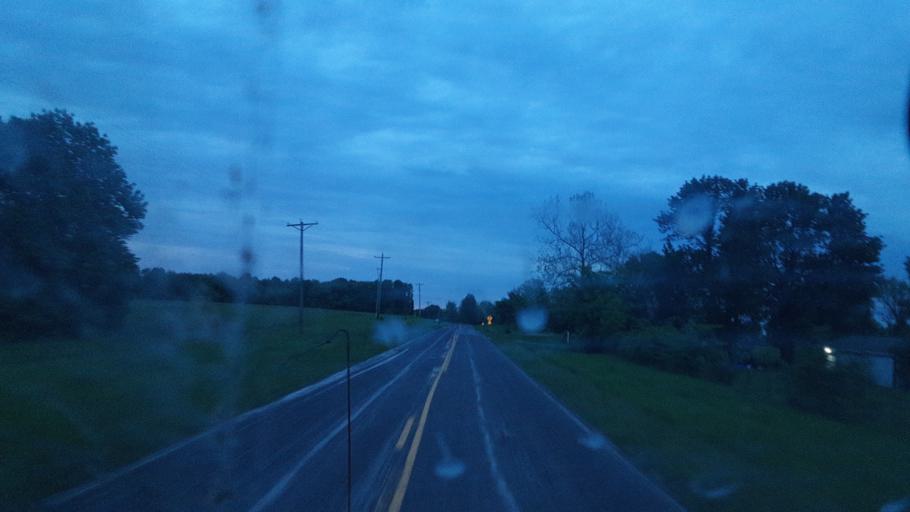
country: US
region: Missouri
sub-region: Clark County
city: Kahoka
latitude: 40.4361
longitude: -91.5926
